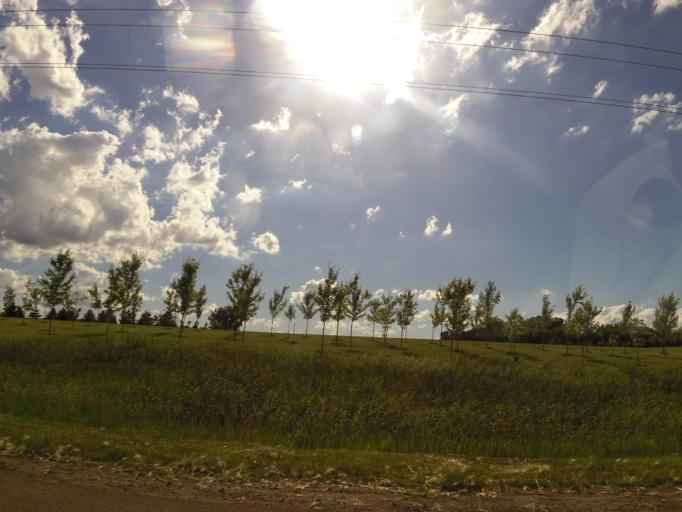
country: US
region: Minnesota
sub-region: Carver County
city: Waconia
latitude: 44.8508
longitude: -93.8193
